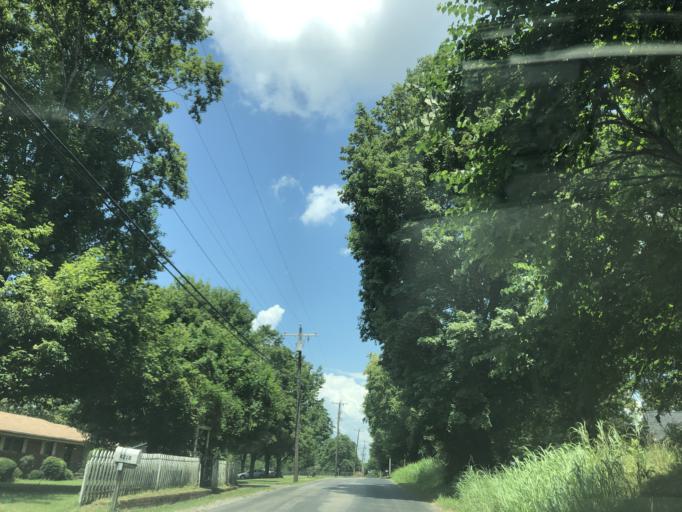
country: US
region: Tennessee
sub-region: Davidson County
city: Lakewood
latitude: 36.2024
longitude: -86.6196
